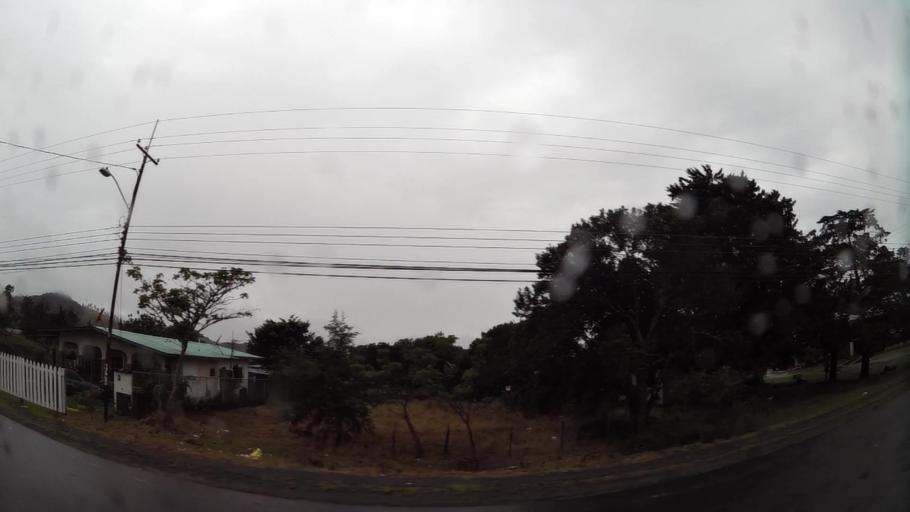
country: PA
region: Chiriqui
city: Volcan
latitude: 8.7719
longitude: -82.6362
